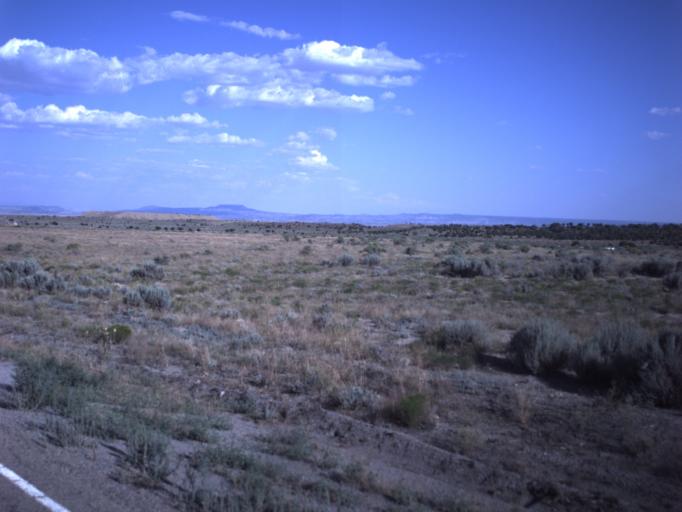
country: US
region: Utah
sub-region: Carbon County
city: Price
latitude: 39.4843
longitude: -110.8951
